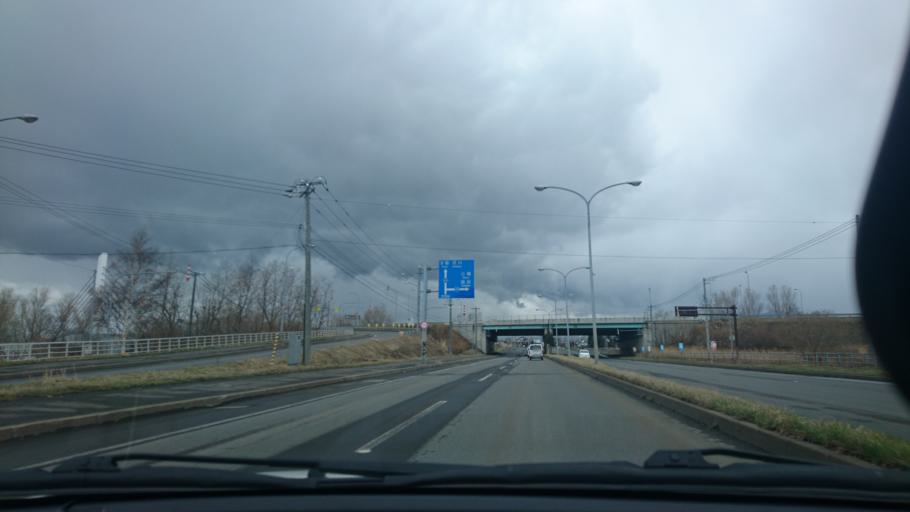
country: JP
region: Hokkaido
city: Ishikari
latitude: 43.1847
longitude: 141.3238
